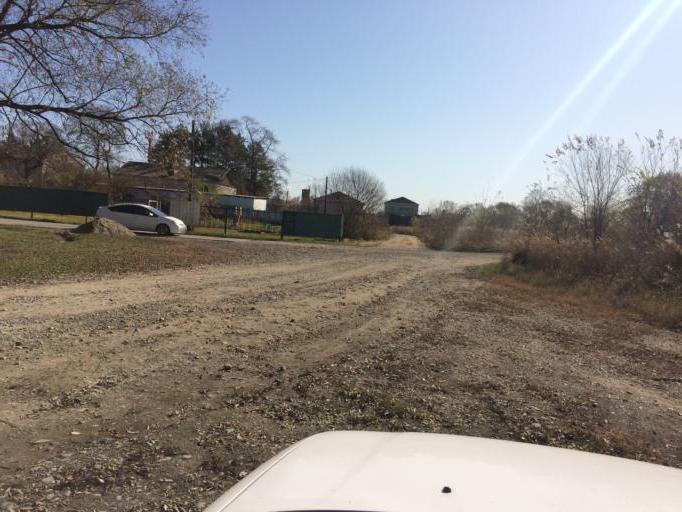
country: RU
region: Primorskiy
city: Dal'nerechensk
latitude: 45.9109
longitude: 133.8027
